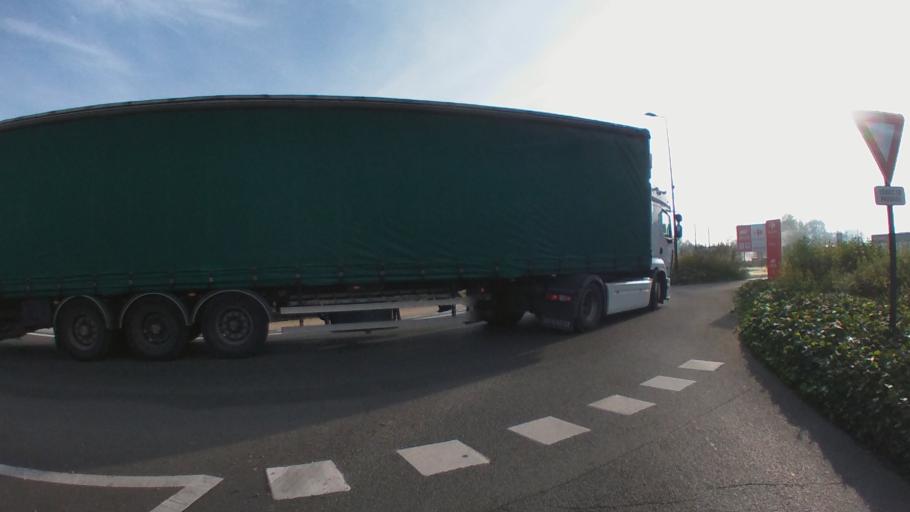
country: FR
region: Pays de la Loire
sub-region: Departement de la Sarthe
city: La Fleche
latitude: 47.7017
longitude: -0.0911
